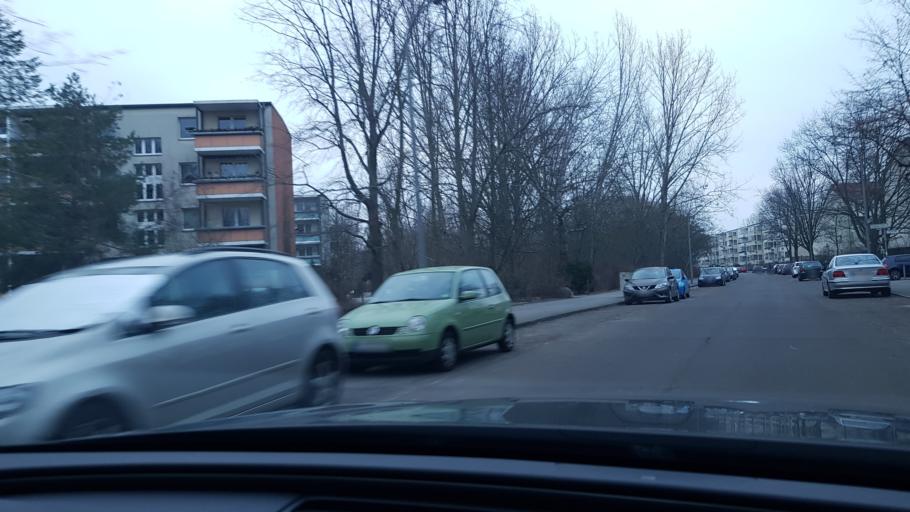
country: DE
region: Berlin
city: Grunau
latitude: 52.4249
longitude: 13.5921
